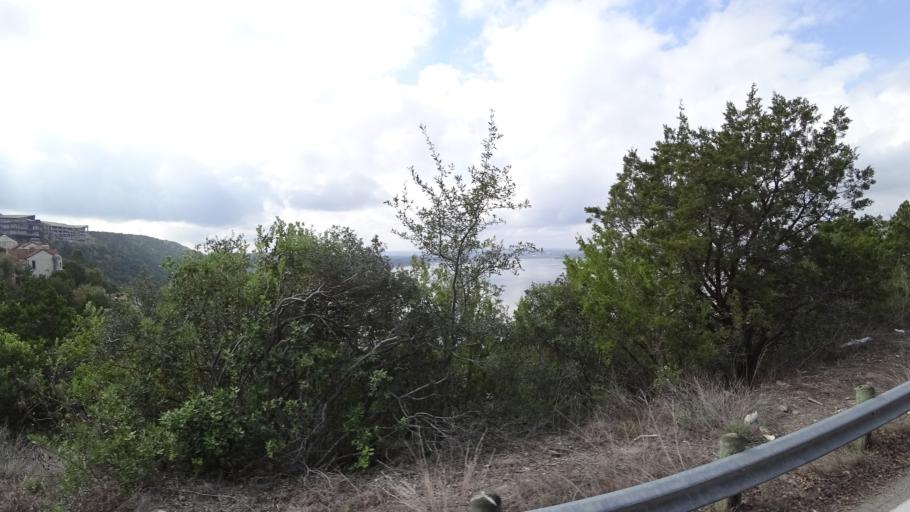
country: US
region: Texas
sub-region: Travis County
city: Hudson Bend
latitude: 30.4098
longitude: -97.8756
